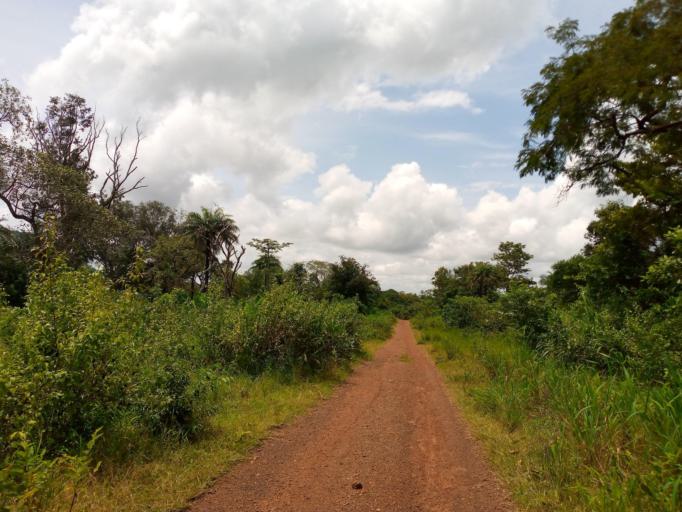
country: SL
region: Northern Province
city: Binkolo
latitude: 9.1150
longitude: -12.1354
